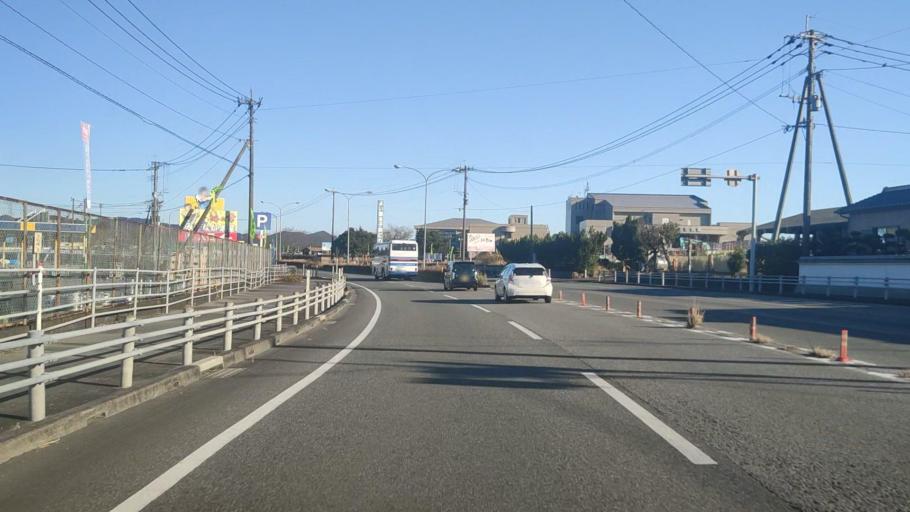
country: JP
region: Miyazaki
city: Nobeoka
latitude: 32.4619
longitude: 131.6486
